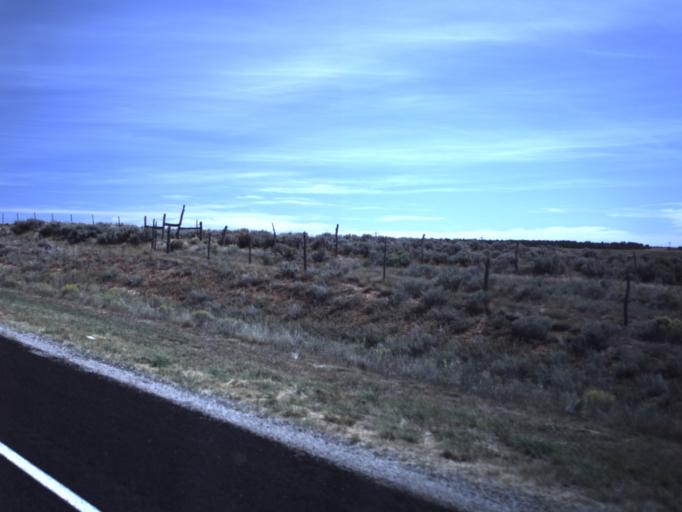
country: US
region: Utah
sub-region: San Juan County
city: Monticello
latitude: 37.8441
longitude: -109.1384
